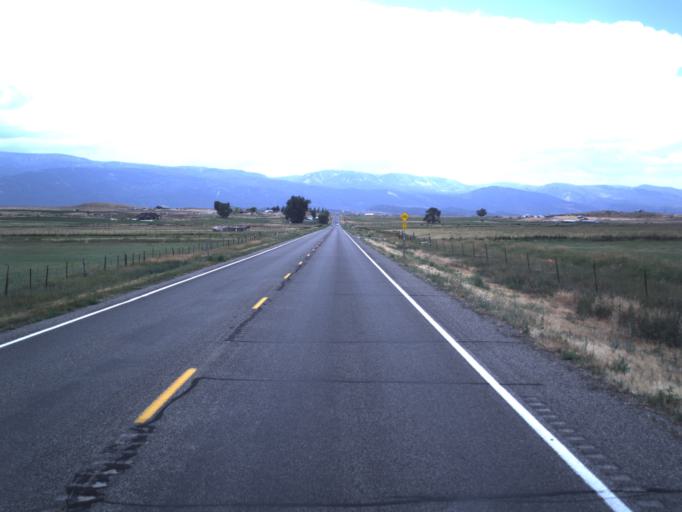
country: US
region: Utah
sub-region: Sanpete County
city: Moroni
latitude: 39.5177
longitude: -111.5733
